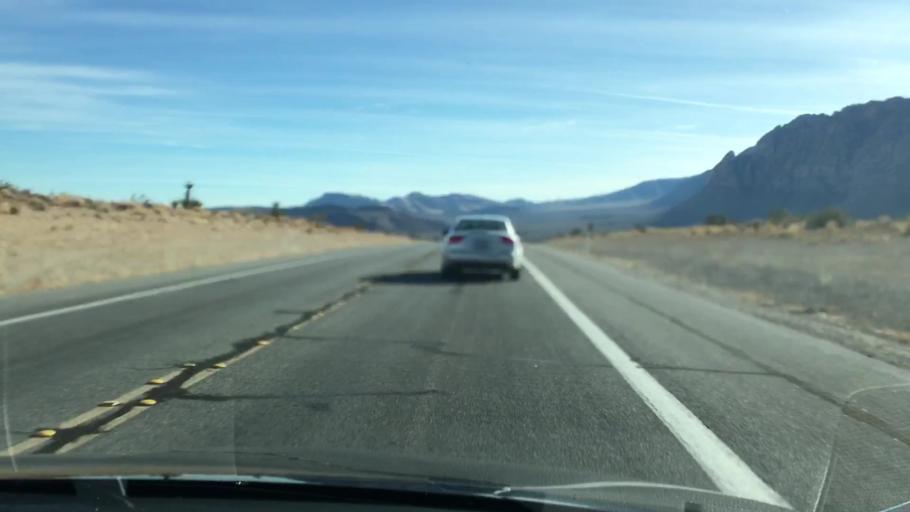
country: US
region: Nevada
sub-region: Clark County
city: Summerlin South
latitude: 36.0981
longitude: -115.4492
